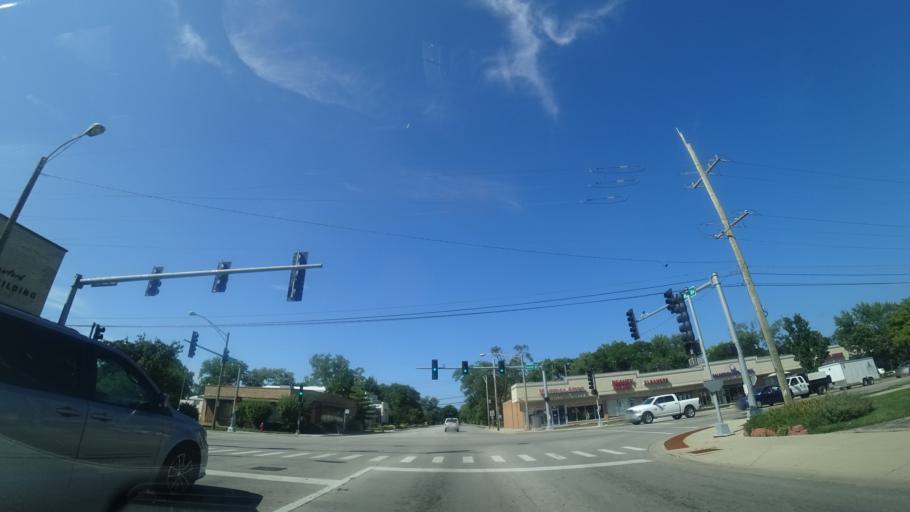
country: US
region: Illinois
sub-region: Cook County
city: Skokie
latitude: 42.0478
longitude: -87.7275
